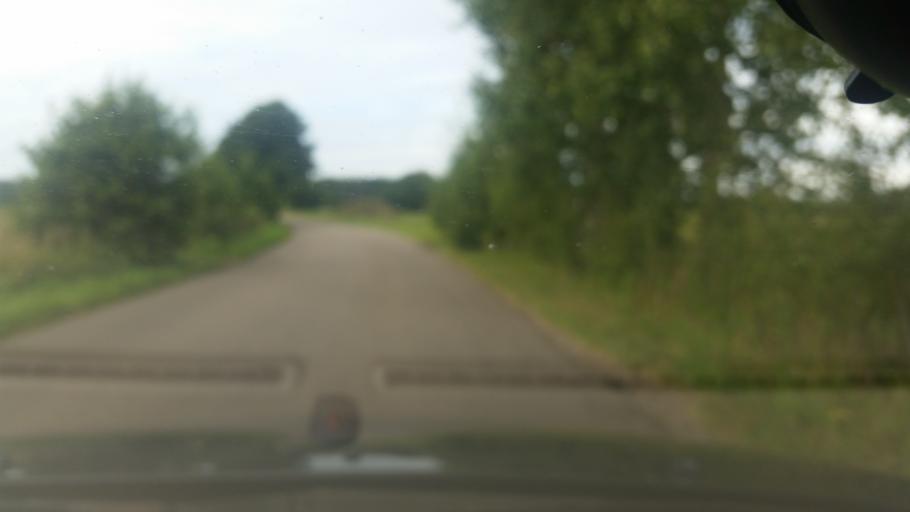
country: PL
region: Pomeranian Voivodeship
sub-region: Powiat leborski
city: Leba
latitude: 54.7342
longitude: 17.6006
